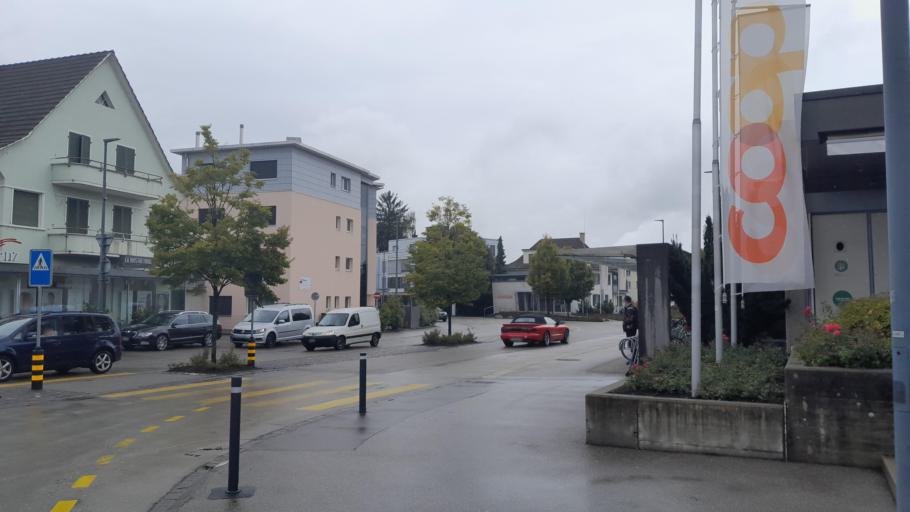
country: CH
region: Solothurn
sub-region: Bezirk Wasseramt
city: Gerlafingen
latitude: 47.1708
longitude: 7.5731
